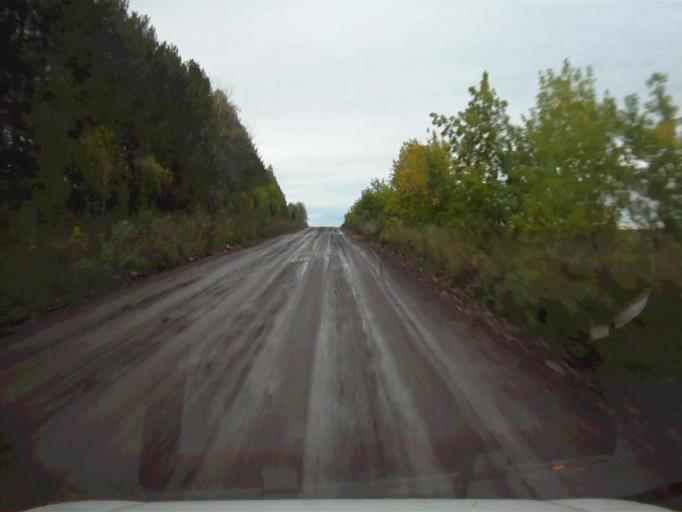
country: RU
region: Sverdlovsk
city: Mikhaylovsk
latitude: 56.1552
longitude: 59.2604
